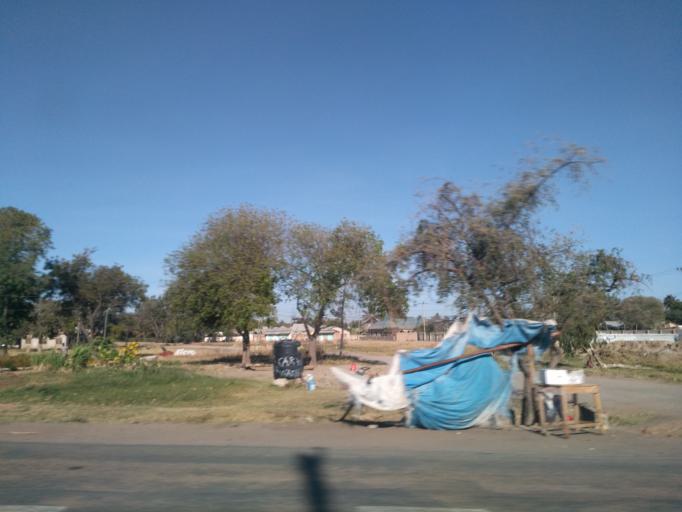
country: TZ
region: Dodoma
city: Dodoma
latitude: -6.1536
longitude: 35.7475
